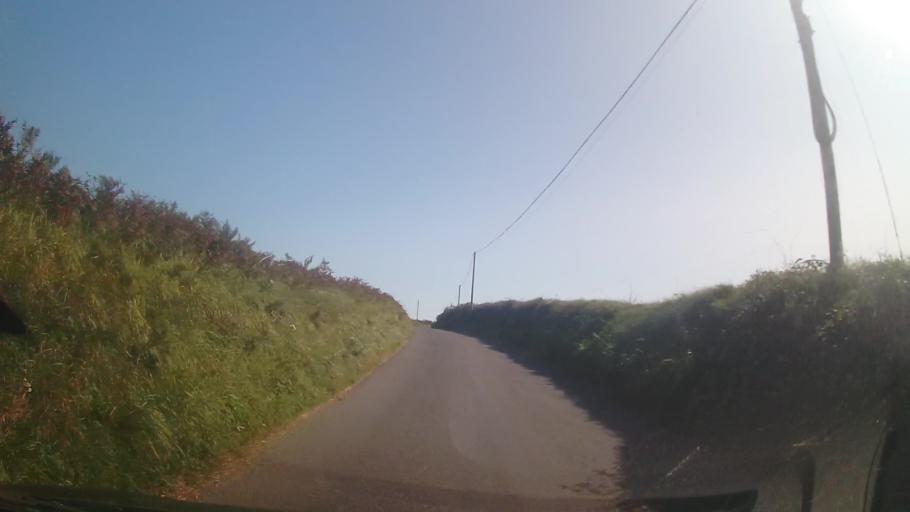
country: GB
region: Wales
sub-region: Pembrokeshire
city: Llanrhian
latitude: 51.9342
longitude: -5.1690
